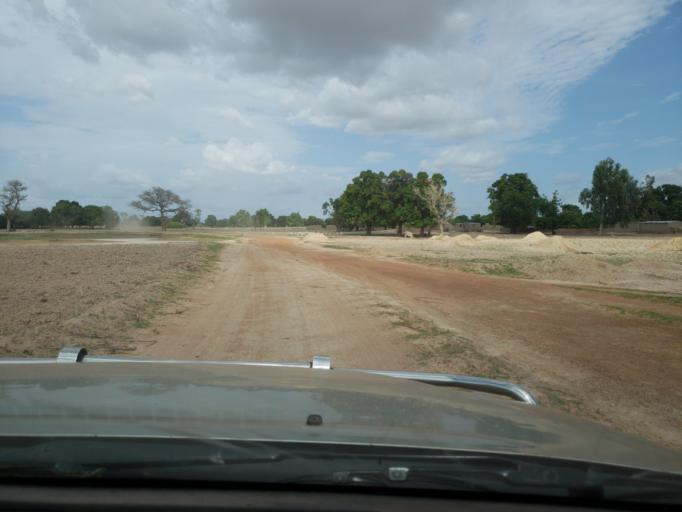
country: ML
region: Segou
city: Bla
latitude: 12.7353
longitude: -5.6635
